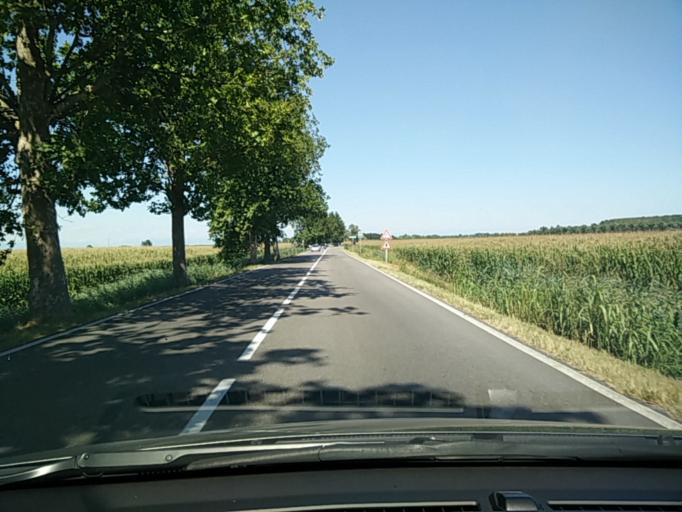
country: IT
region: Veneto
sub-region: Provincia di Venezia
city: La Salute di Livenza
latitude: 45.6804
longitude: 12.8195
